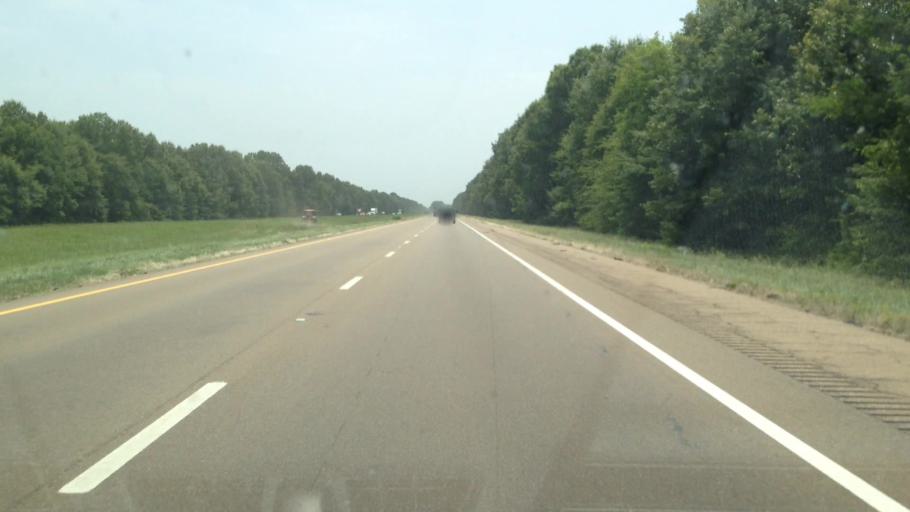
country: US
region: Texas
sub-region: Morris County
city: Naples
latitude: 33.3319
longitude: -94.6729
